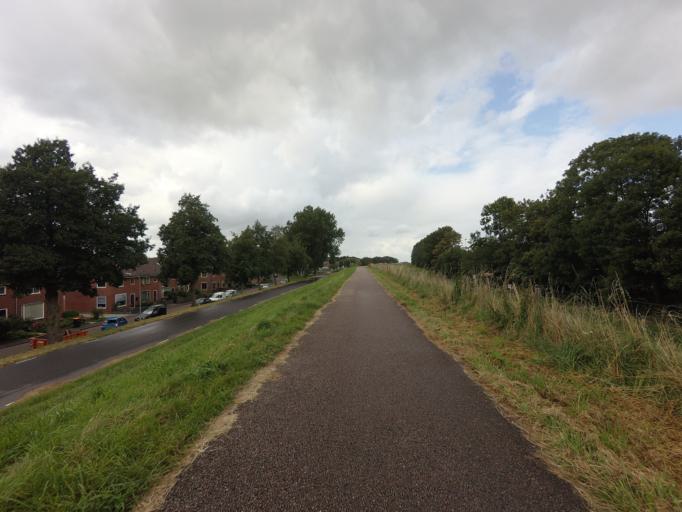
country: NL
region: North Holland
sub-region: Gemeente Enkhuizen
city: Enkhuizen
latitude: 52.7142
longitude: 5.2828
